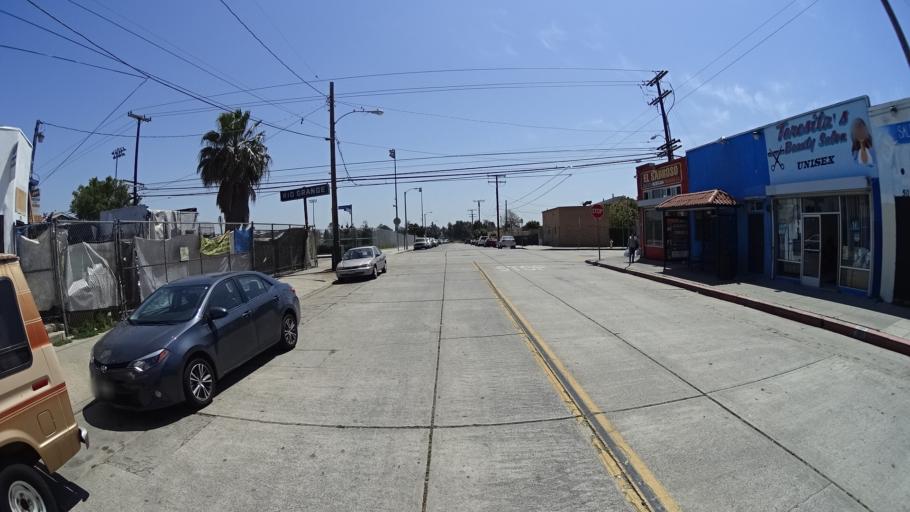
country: US
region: California
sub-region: Los Angeles County
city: Belvedere
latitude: 34.0427
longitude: -118.1778
